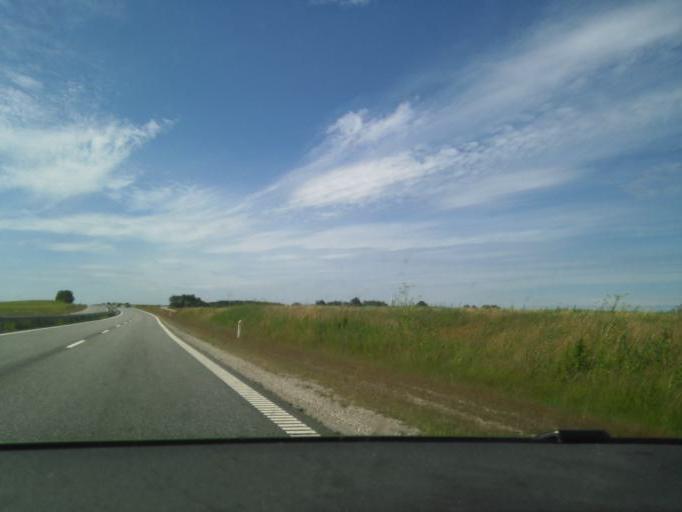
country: DK
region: Zealand
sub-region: Holbaek Kommune
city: Vipperod
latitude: 55.6455
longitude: 11.7440
